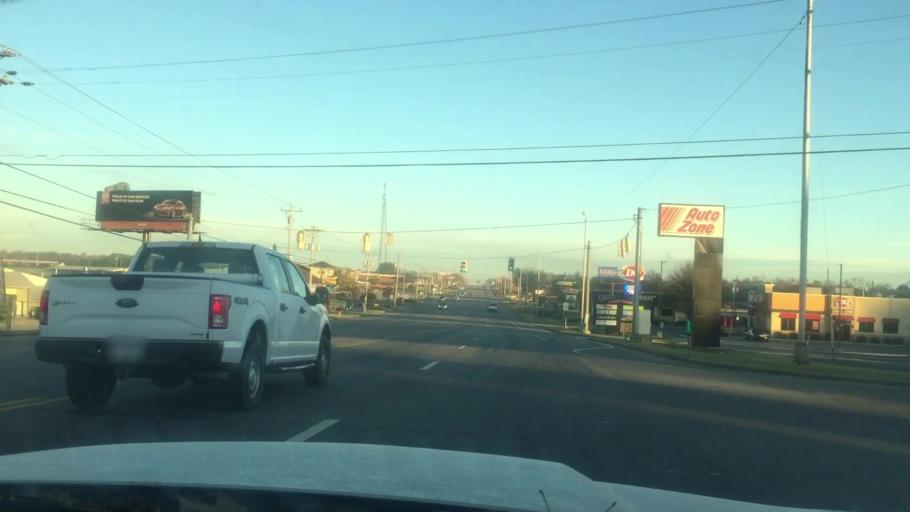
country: US
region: Tennessee
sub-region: Franklin County
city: Decherd
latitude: 35.2090
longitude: -86.0948
